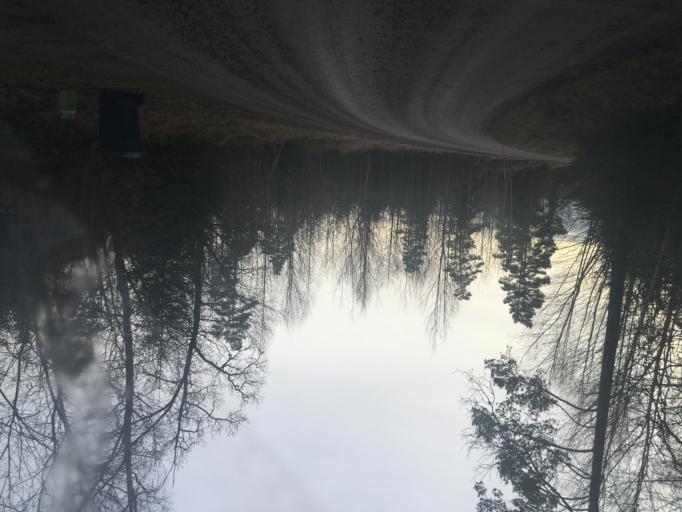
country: SE
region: OEstergoetland
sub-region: Norrkopings Kommun
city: Kimstad
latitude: 58.4196
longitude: 16.0444
